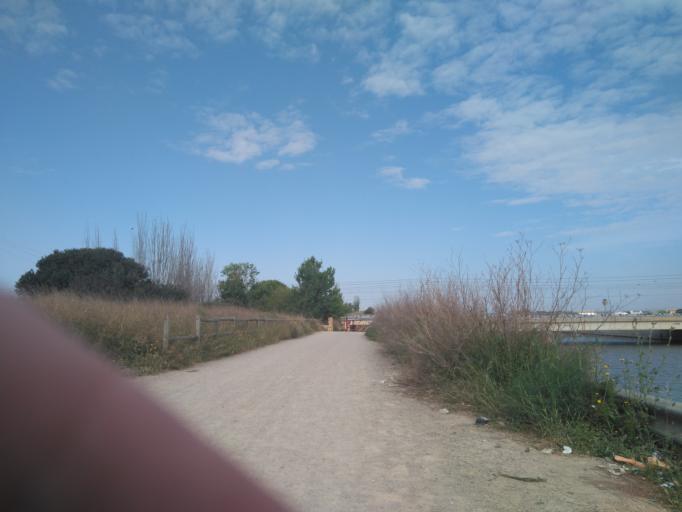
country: ES
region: Valencia
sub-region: Provincia de Valencia
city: Alboraya
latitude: 39.5018
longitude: -0.3273
